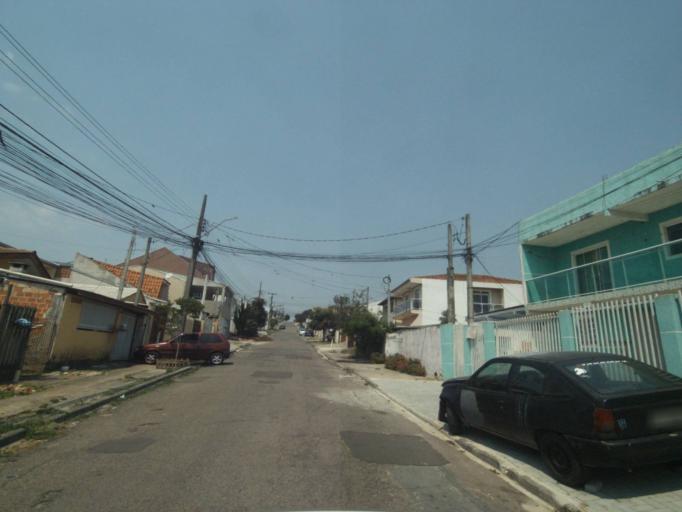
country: BR
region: Parana
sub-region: Sao Jose Dos Pinhais
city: Sao Jose dos Pinhais
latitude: -25.5397
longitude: -49.2464
